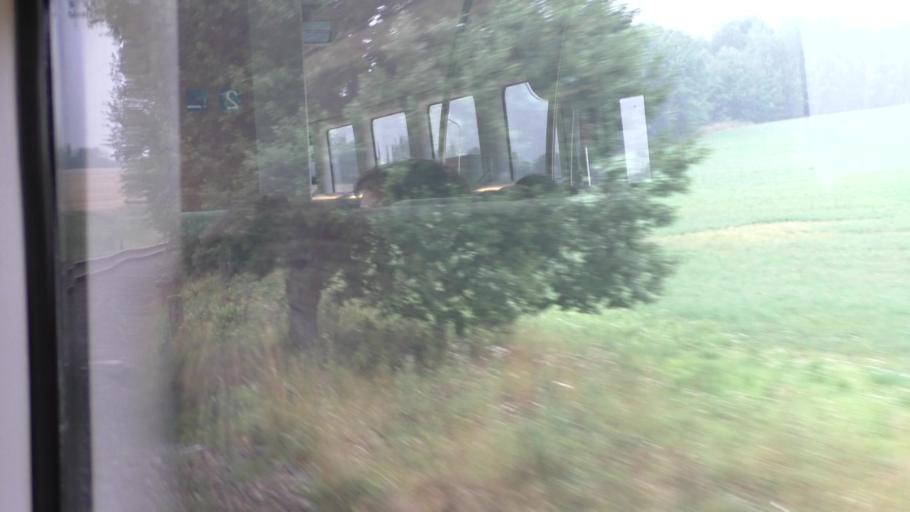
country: DE
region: Saxony
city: Eibau
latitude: 50.9668
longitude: 14.6674
